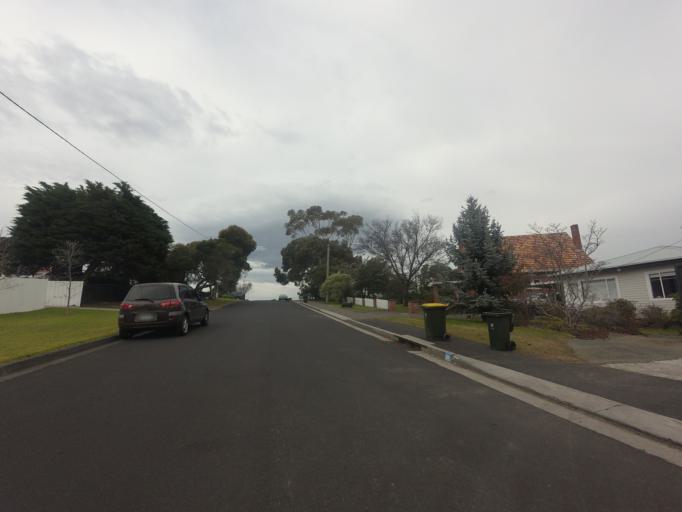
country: AU
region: Tasmania
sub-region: Clarence
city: Bellerive
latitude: -42.8807
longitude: 147.3870
